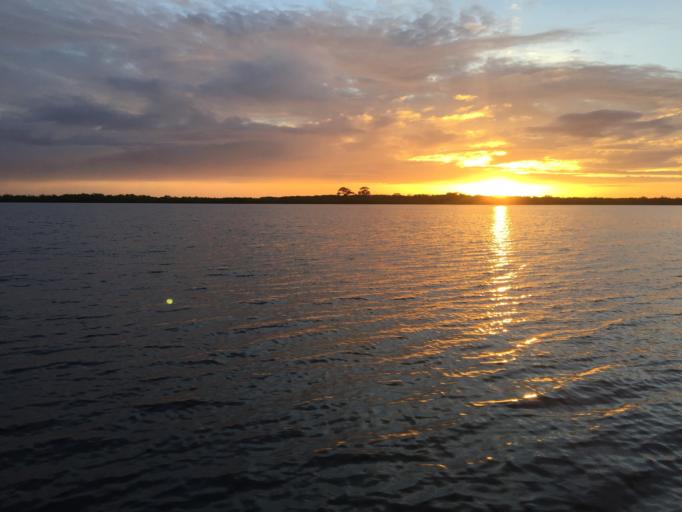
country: SN
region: Fatick
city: Sokone
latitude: 13.8288
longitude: -16.4946
